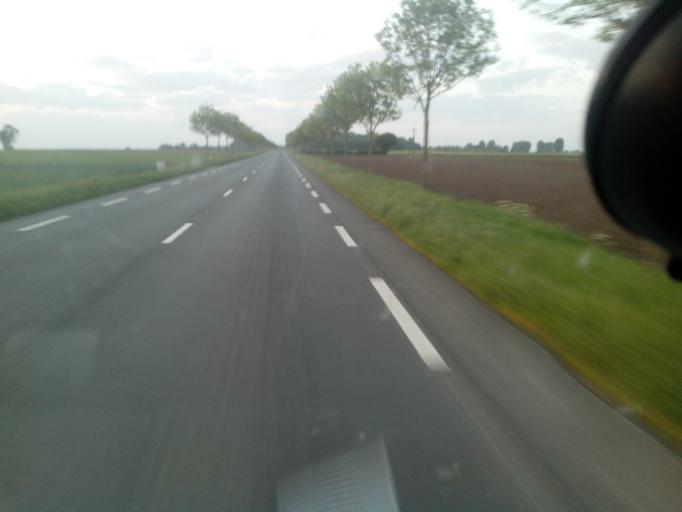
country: FR
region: Nord-Pas-de-Calais
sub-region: Departement du Pas-de-Calais
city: Marconnelle
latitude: 50.2981
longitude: 2.0005
